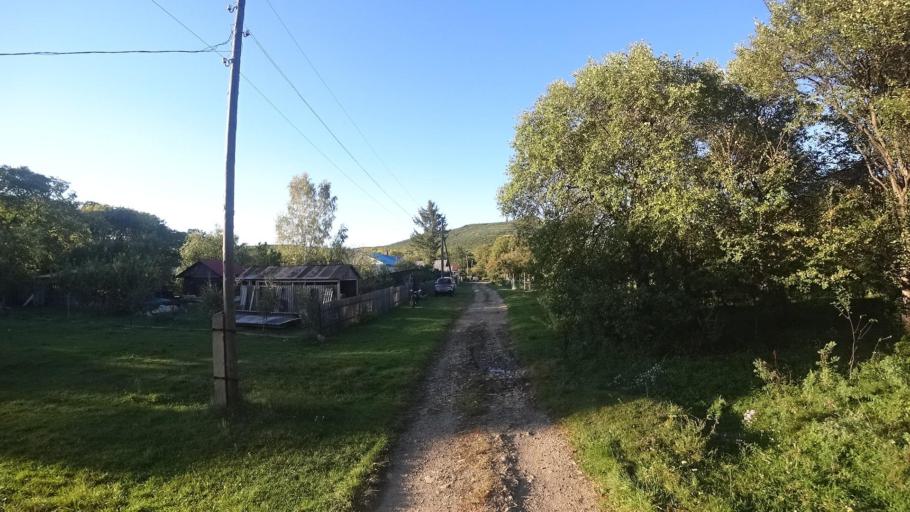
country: RU
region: Primorskiy
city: Kirovskiy
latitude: 44.8270
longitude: 133.5668
